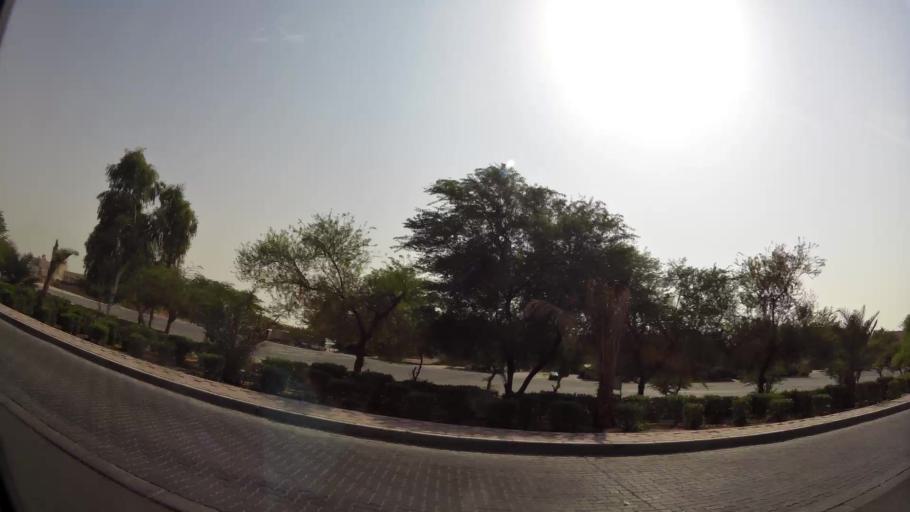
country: KW
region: Muhafazat al Jahra'
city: Al Jahra'
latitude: 29.3369
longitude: 47.6599
